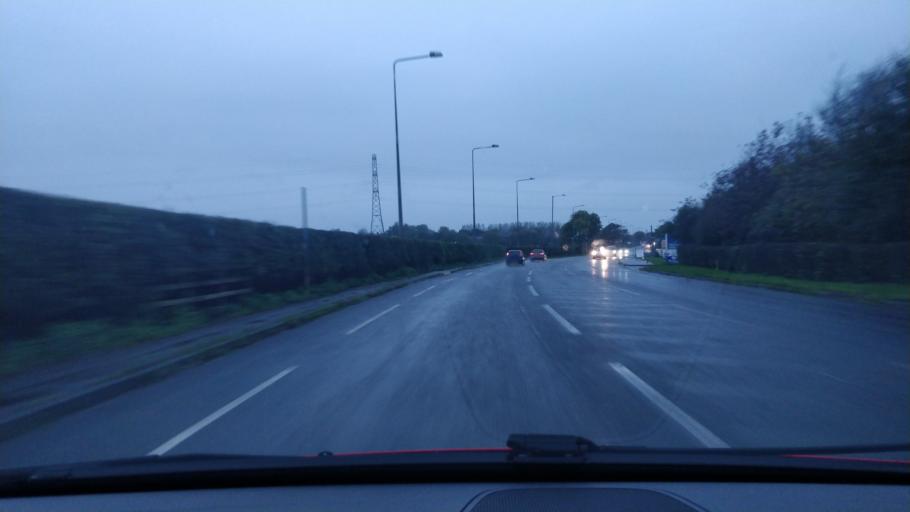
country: GB
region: England
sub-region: Lancashire
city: Poulton le Fylde
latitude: 53.7859
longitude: -2.9671
